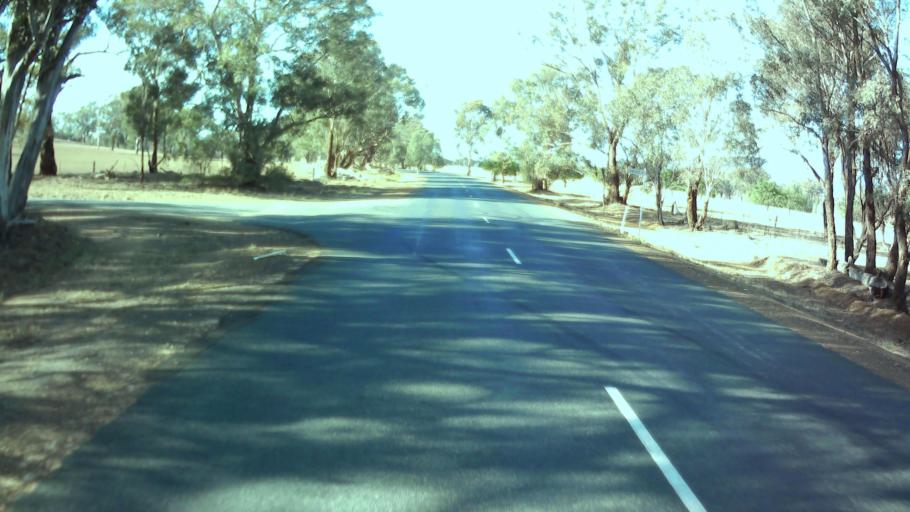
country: AU
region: New South Wales
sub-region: Weddin
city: Grenfell
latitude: -33.9416
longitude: 148.1362
